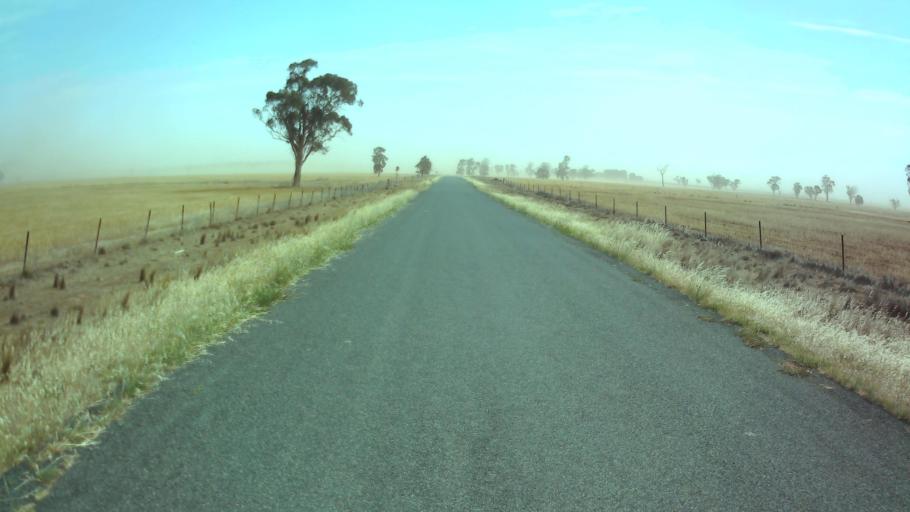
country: AU
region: New South Wales
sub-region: Weddin
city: Grenfell
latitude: -33.7418
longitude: 147.9925
